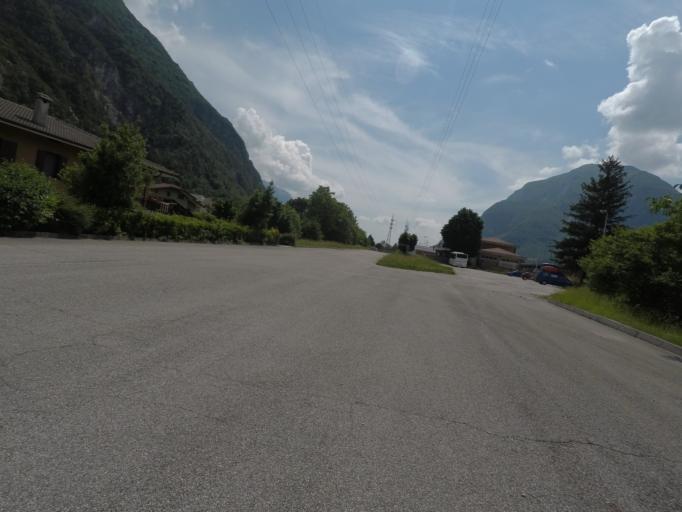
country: IT
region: Friuli Venezia Giulia
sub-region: Provincia di Udine
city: Amaro
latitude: 46.3747
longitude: 13.1337
